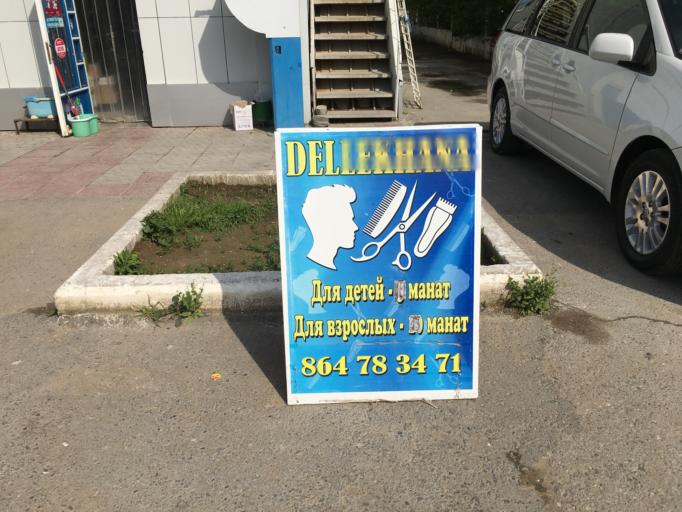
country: TM
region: Ahal
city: Ashgabat
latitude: 37.9235
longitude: 58.4206
